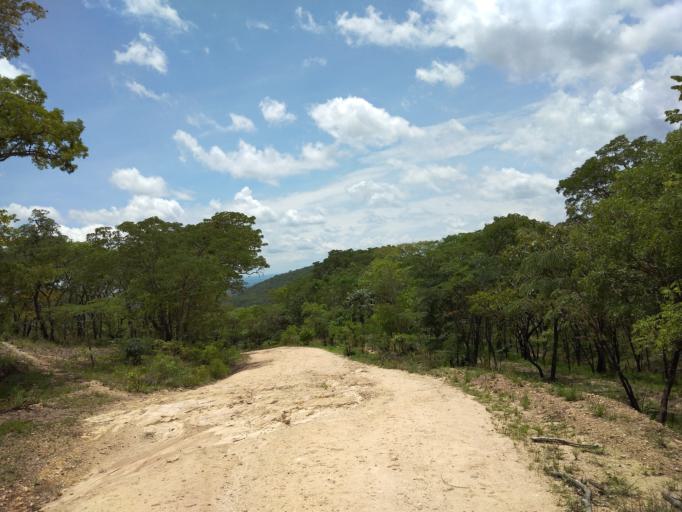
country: ZM
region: Central
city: Mkushi
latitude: -13.9323
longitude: 29.8625
